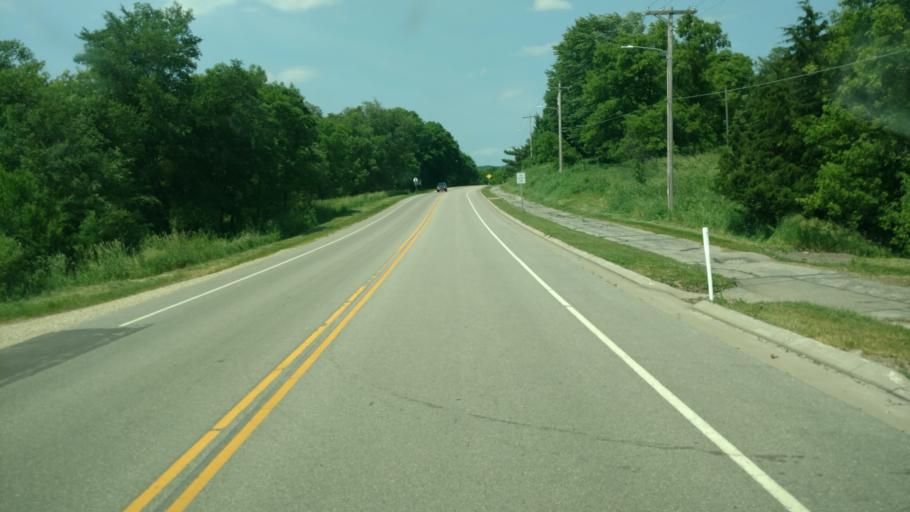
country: US
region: Wisconsin
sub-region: Vernon County
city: Viroqua
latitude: 43.4959
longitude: -90.6801
